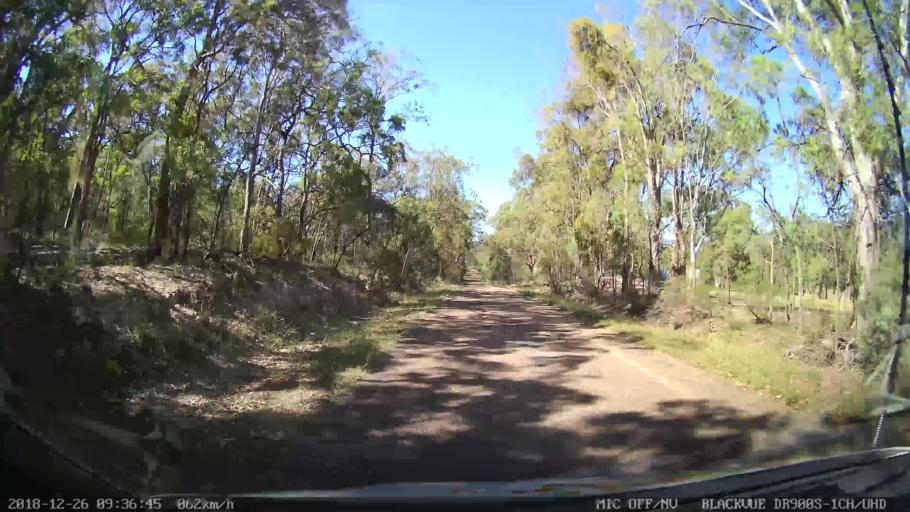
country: AU
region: New South Wales
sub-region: Mid-Western Regional
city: Kandos
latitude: -32.9266
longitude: 150.0397
